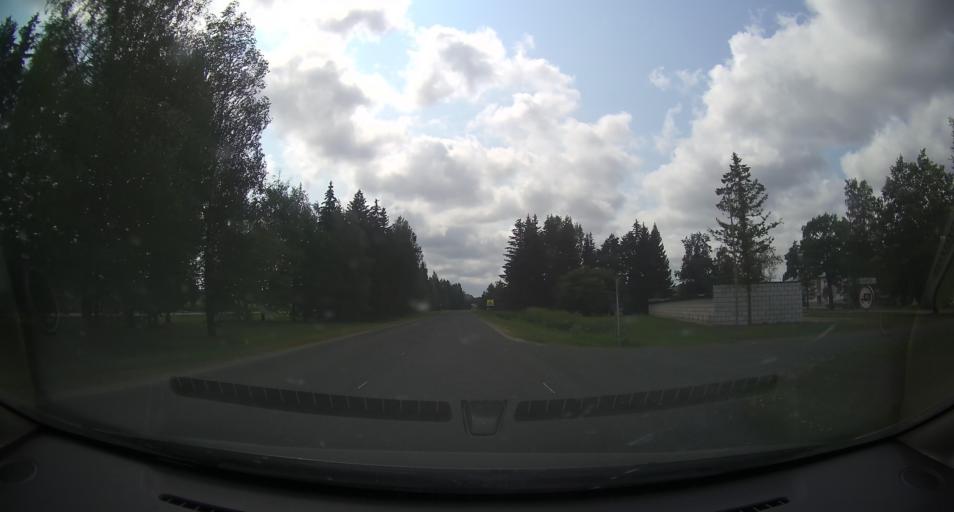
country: EE
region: Paernumaa
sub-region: Audru vald
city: Audru
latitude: 58.4761
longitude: 24.3282
